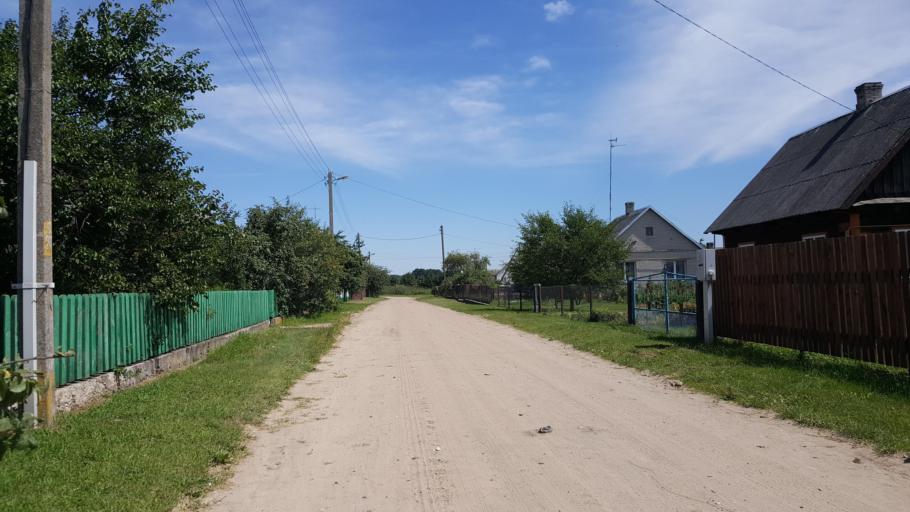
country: BY
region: Brest
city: Pruzhany
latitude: 52.5654
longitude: 24.2212
